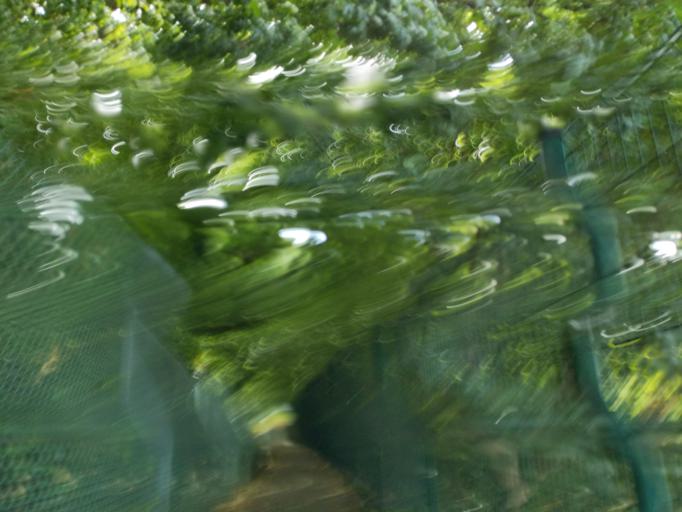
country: GB
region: England
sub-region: Greater London
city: West Wickham
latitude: 51.3769
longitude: -0.0017
